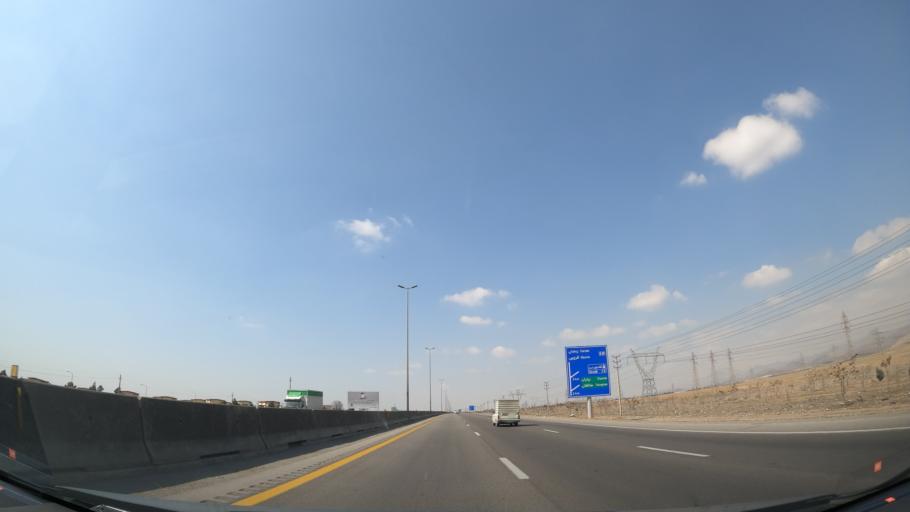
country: IR
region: Qazvin
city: Abyek
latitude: 36.0685
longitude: 50.4827
